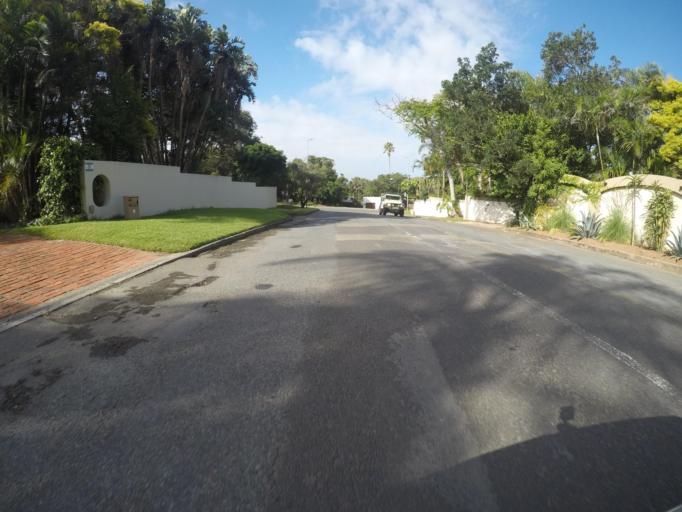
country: ZA
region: Eastern Cape
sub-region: Buffalo City Metropolitan Municipality
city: East London
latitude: -32.9722
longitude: 27.9586
